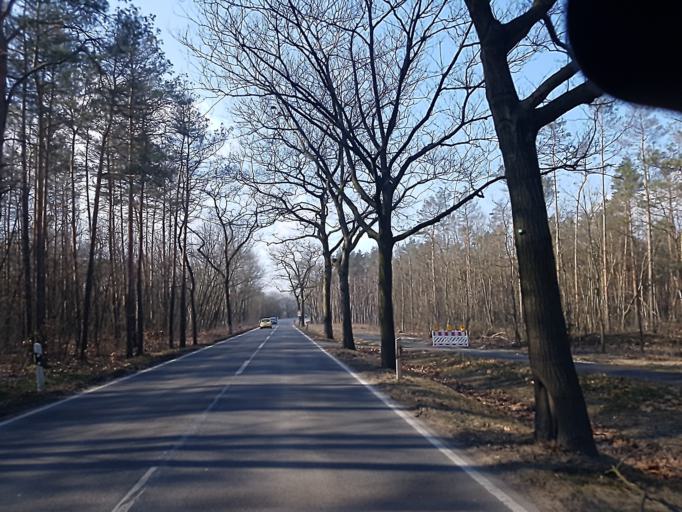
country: DE
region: Brandenburg
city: Doberlug-Kirchhain
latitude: 51.6302
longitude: 13.5975
